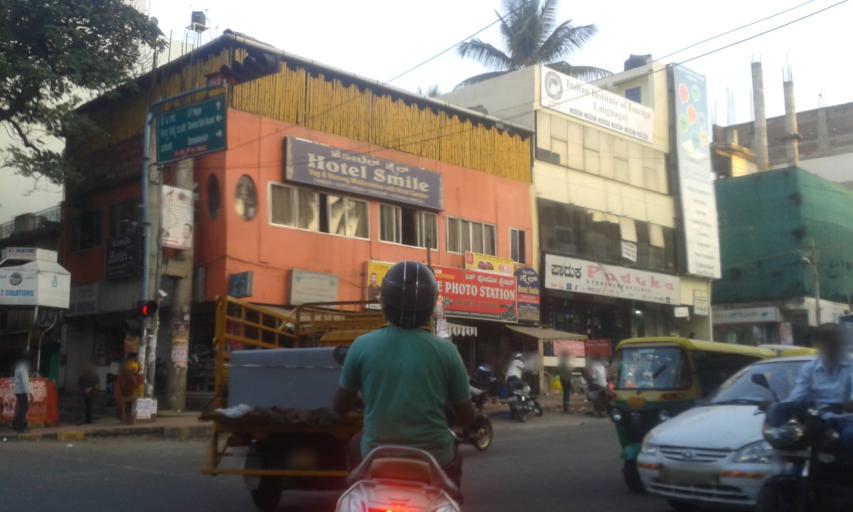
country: IN
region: Karnataka
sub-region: Bangalore Urban
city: Bangalore
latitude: 12.9169
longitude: 77.5950
